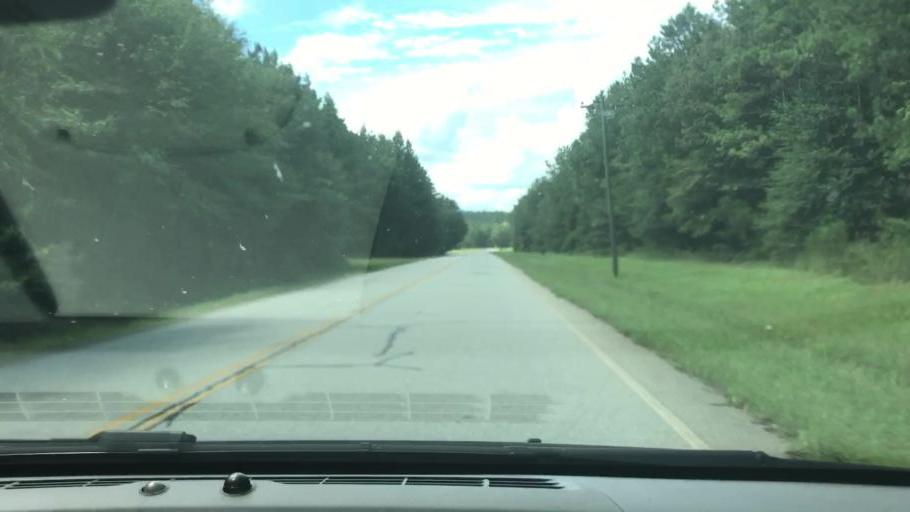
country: US
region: Georgia
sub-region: Stewart County
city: Lumpkin
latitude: 32.1433
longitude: -84.9309
